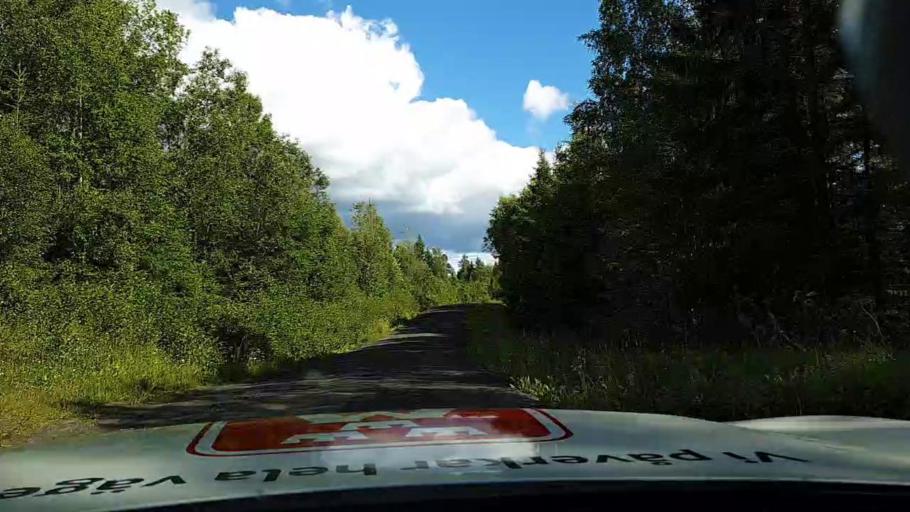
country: SE
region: Jaemtland
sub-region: Krokoms Kommun
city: Valla
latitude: 63.3214
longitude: 13.7573
